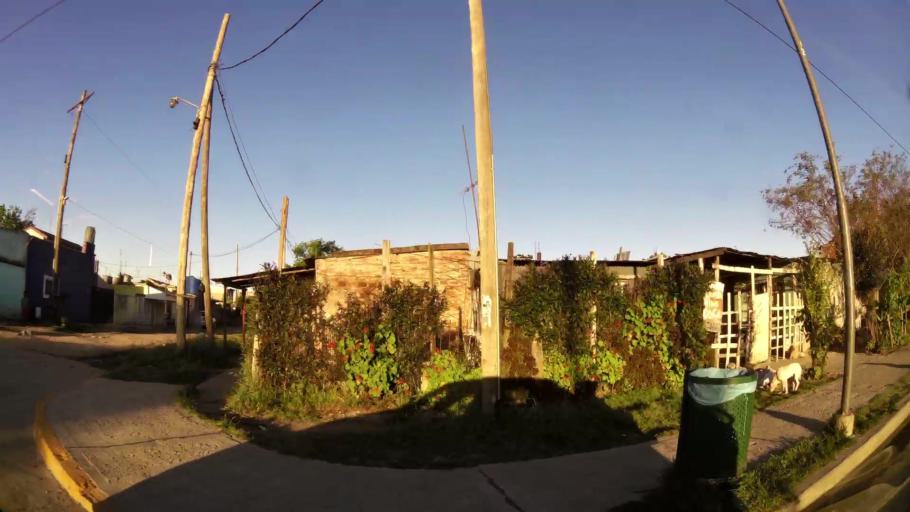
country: AR
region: Buenos Aires
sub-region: Partido de Almirante Brown
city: Adrogue
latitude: -34.7804
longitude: -58.3391
